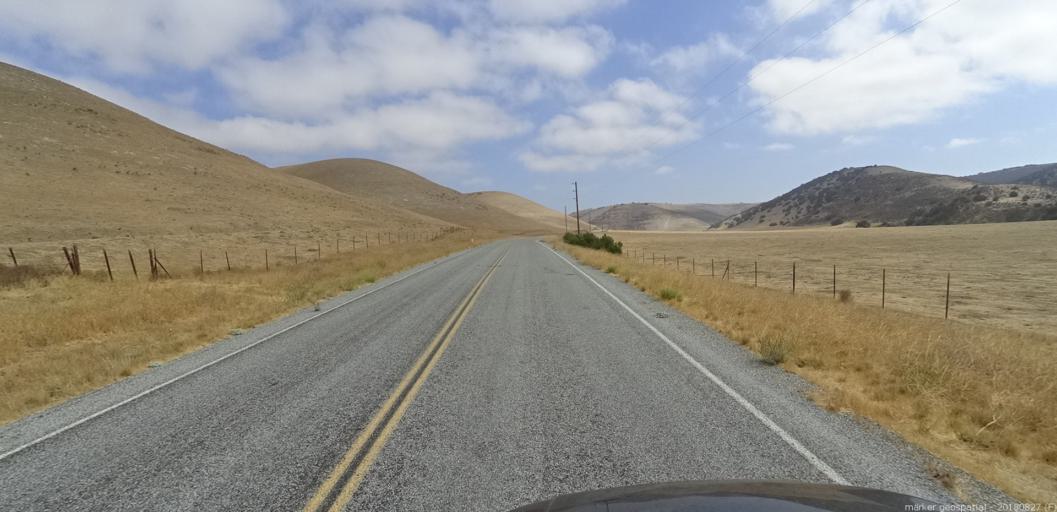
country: US
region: California
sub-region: Monterey County
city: King City
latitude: 36.2785
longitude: -121.0635
